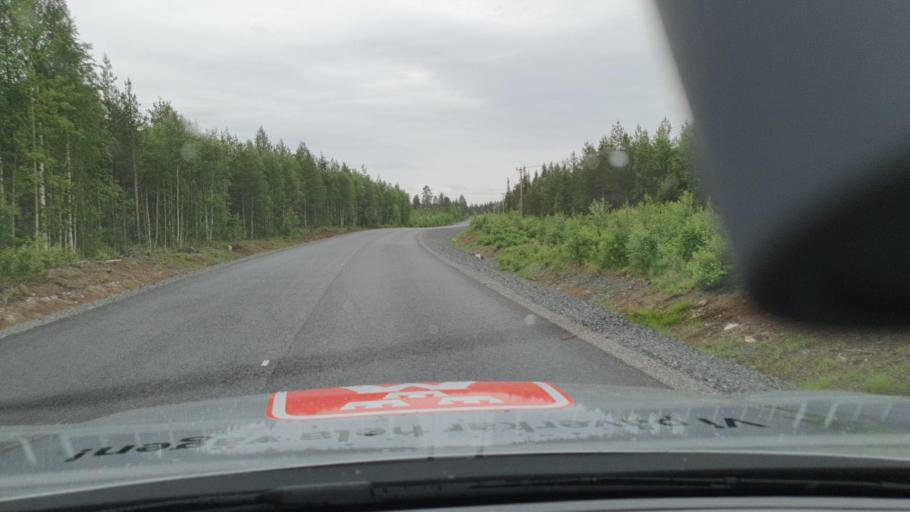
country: SE
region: Norrbotten
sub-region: Overkalix Kommun
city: OEverkalix
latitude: 66.7211
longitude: 23.1867
